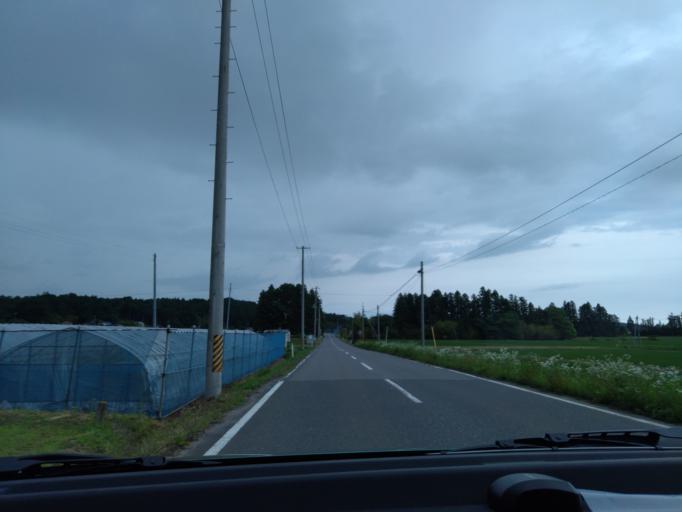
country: JP
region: Iwate
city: Ichinoseki
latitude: 38.8244
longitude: 140.9529
